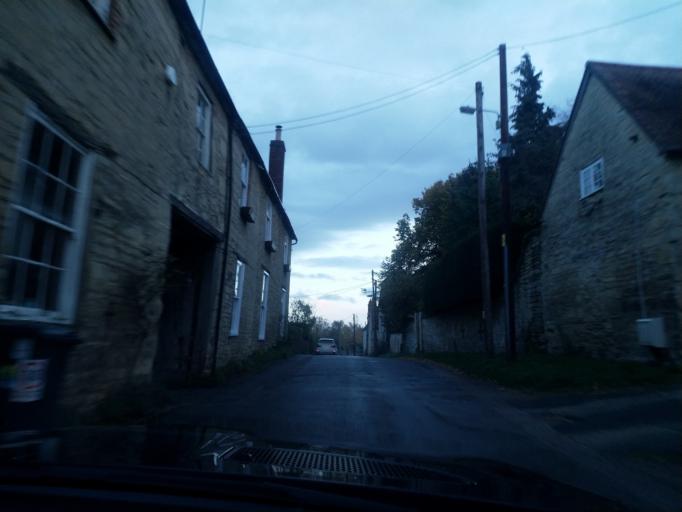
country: GB
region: England
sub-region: Oxfordshire
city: Wheatley
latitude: 51.7460
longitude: -1.1337
